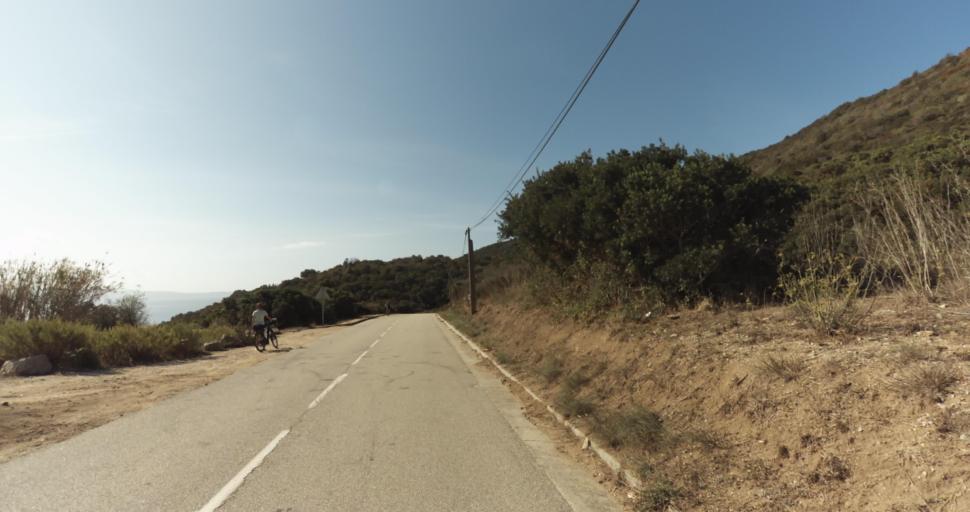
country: FR
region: Corsica
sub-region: Departement de la Corse-du-Sud
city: Ajaccio
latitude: 41.9217
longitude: 8.6425
